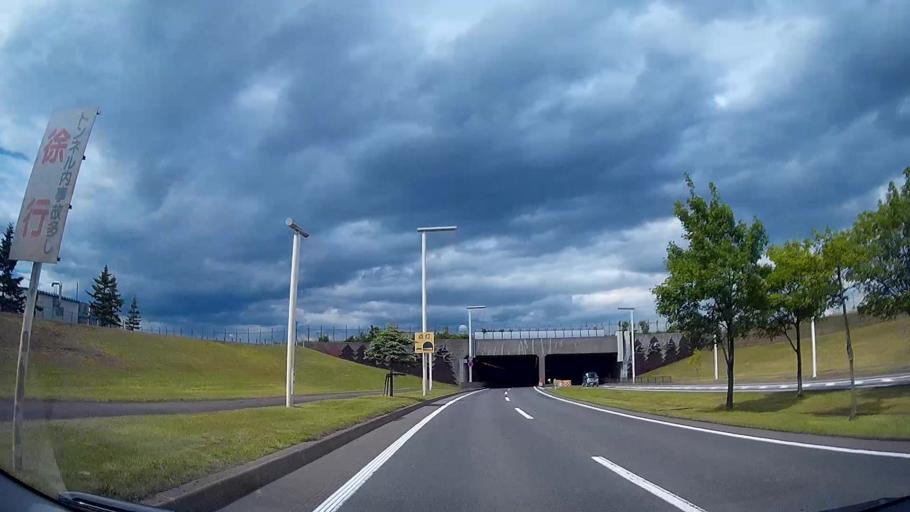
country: JP
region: Hokkaido
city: Chitose
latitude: 42.7897
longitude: 141.6763
